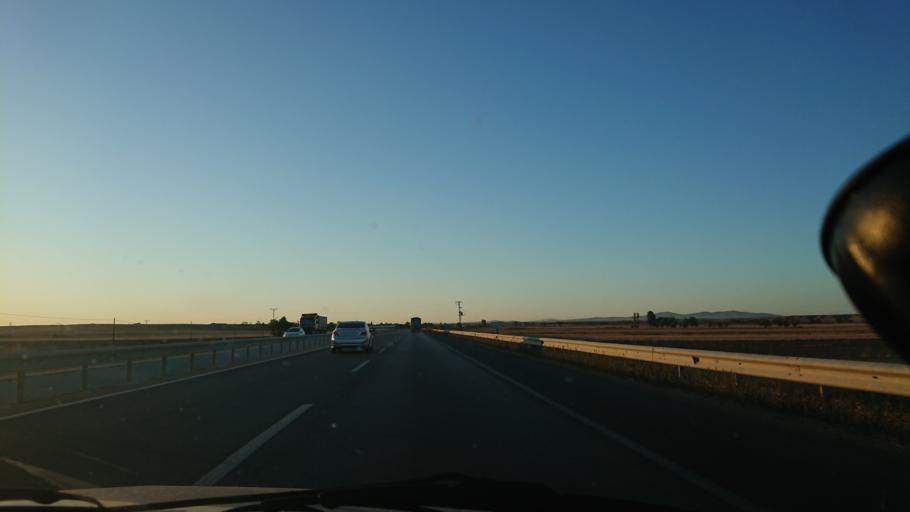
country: TR
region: Eskisehir
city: Mahmudiye
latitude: 39.5275
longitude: 30.9525
